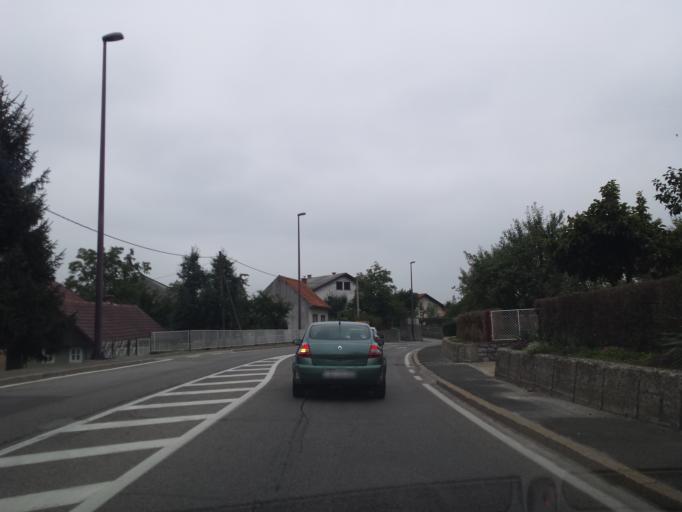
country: HR
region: Karlovacka
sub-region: Grad Karlovac
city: Karlovac
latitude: 45.4710
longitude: 15.5403
